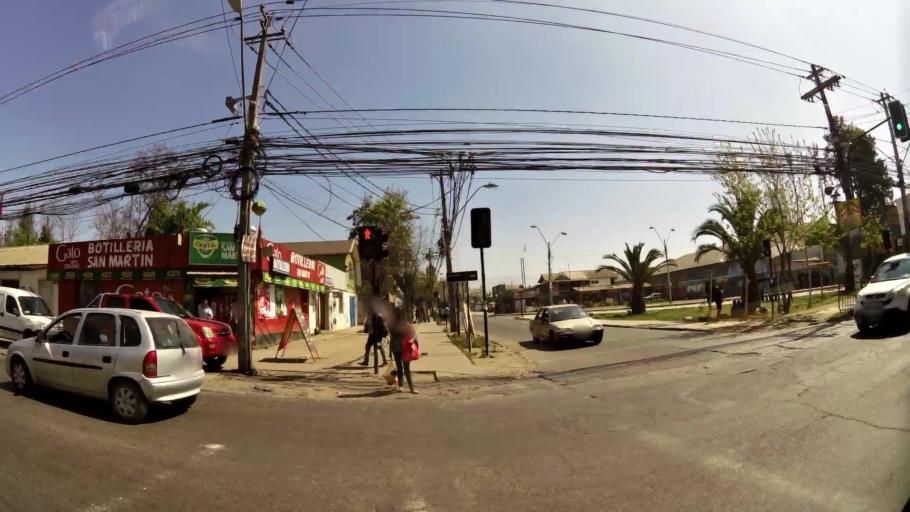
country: CL
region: Santiago Metropolitan
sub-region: Provincia de Santiago
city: Lo Prado
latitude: -33.3667
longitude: -70.7379
